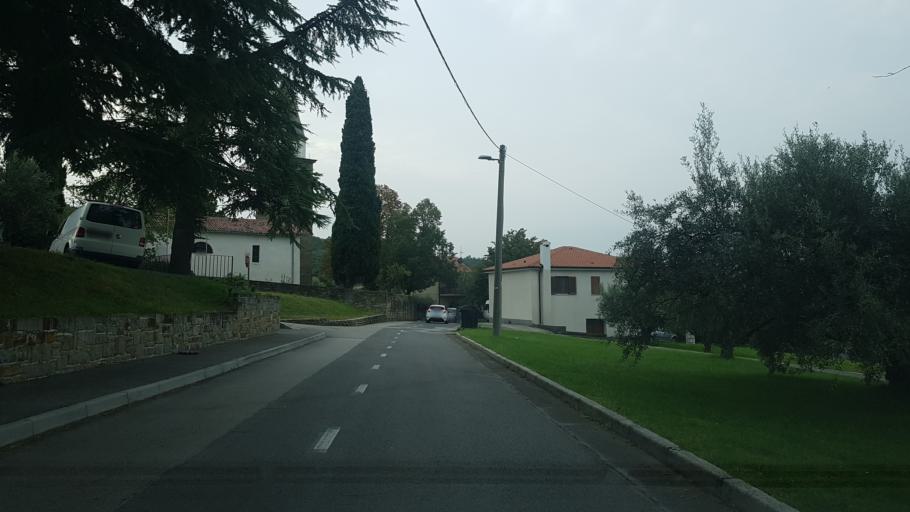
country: SI
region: Koper-Capodistria
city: Spodnje Skofije
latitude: 45.5744
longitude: 13.8030
